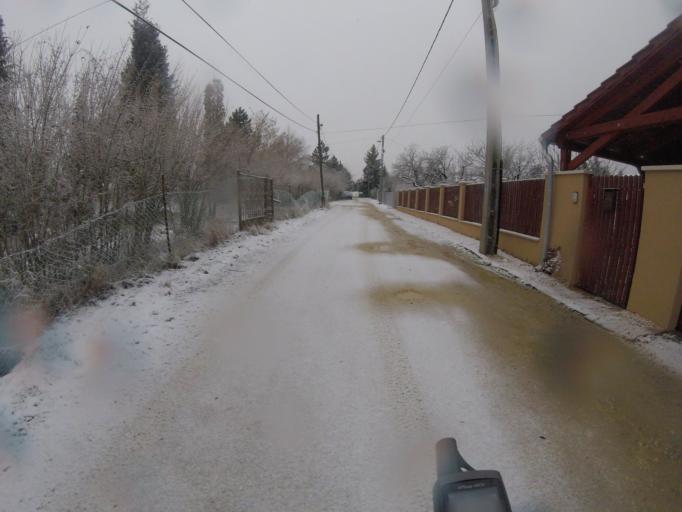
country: HU
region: Pest
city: Pilisszentivan
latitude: 47.5886
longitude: 18.8988
